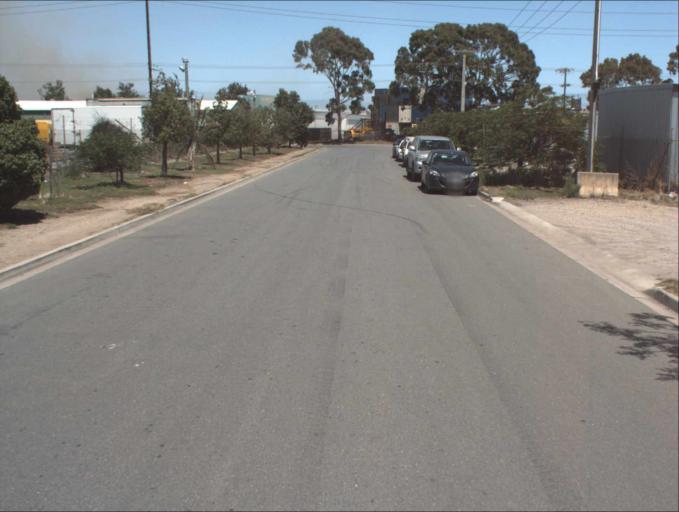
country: AU
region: South Australia
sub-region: Port Adelaide Enfield
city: Alberton
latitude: -34.8376
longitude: 138.5333
